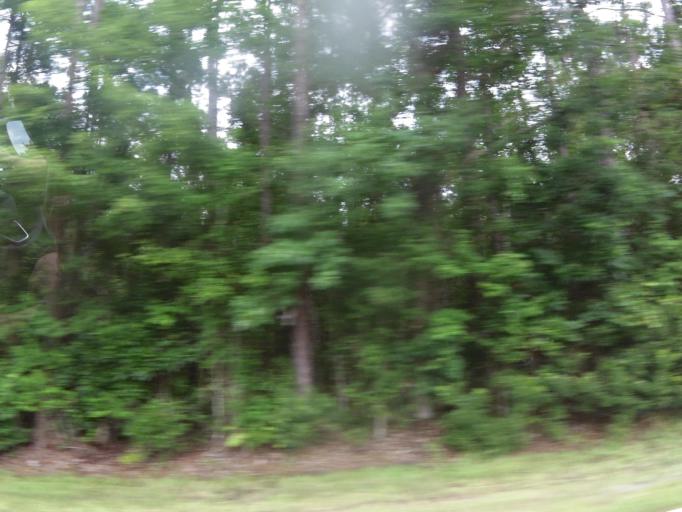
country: US
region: Florida
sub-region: Duval County
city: Jacksonville Beach
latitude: 30.2593
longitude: -81.4565
